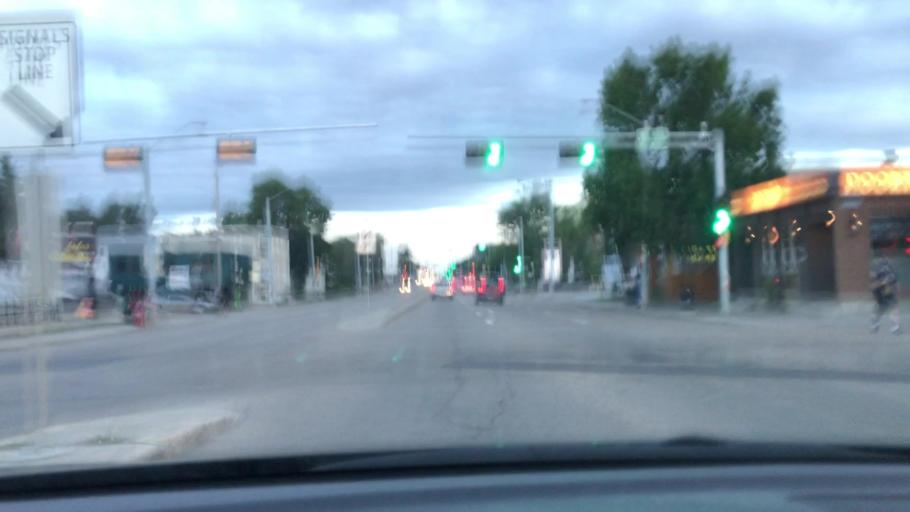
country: CA
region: Alberta
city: Edmonton
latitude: 53.5211
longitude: -113.5121
